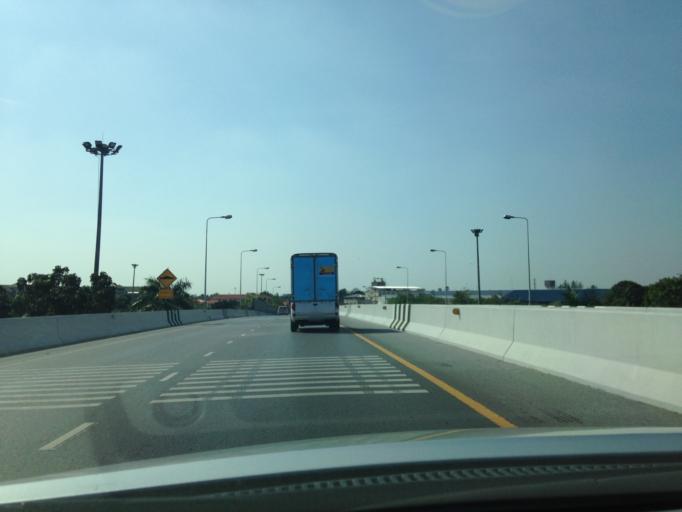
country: TH
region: Nonthaburi
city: Bang Yai
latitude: 13.8223
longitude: 100.4127
